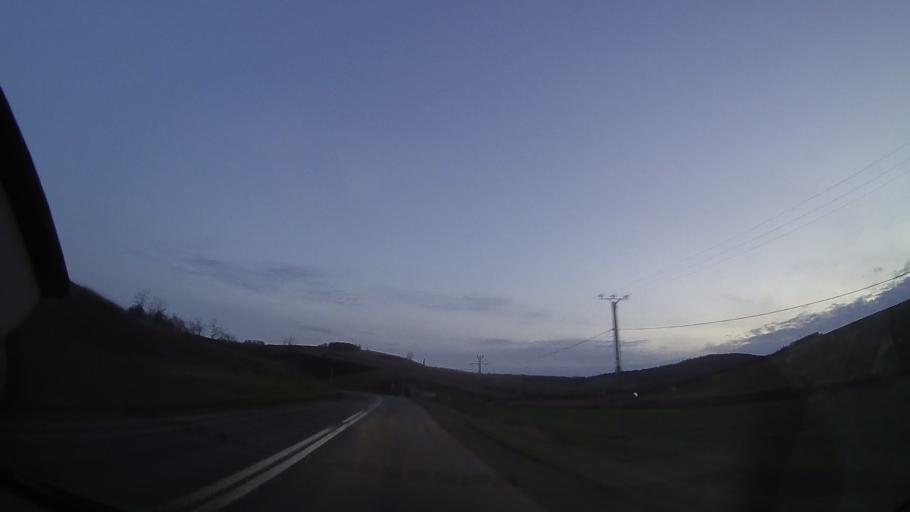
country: RO
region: Cluj
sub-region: Comuna Camarasu
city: Camarasu
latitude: 46.7997
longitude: 24.1643
